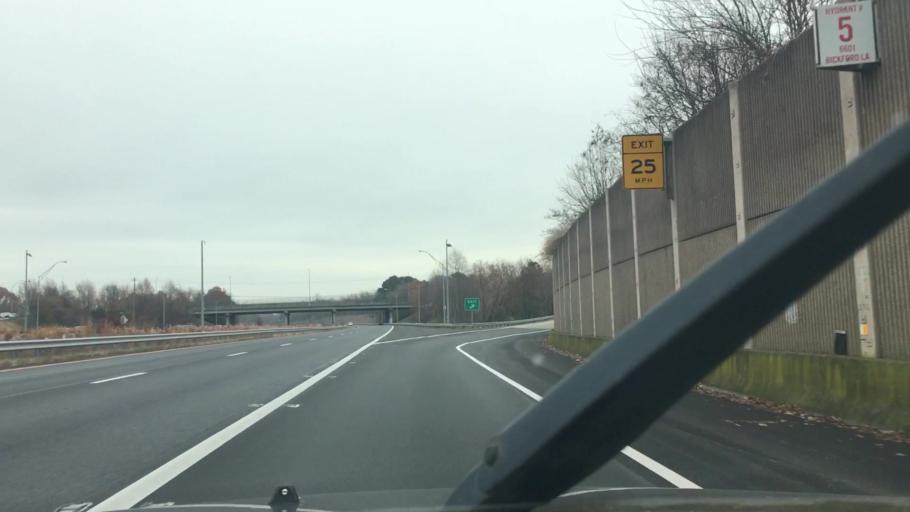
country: US
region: Virginia
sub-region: City of Portsmouth
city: Portsmouth Heights
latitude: 36.8693
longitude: -76.4047
